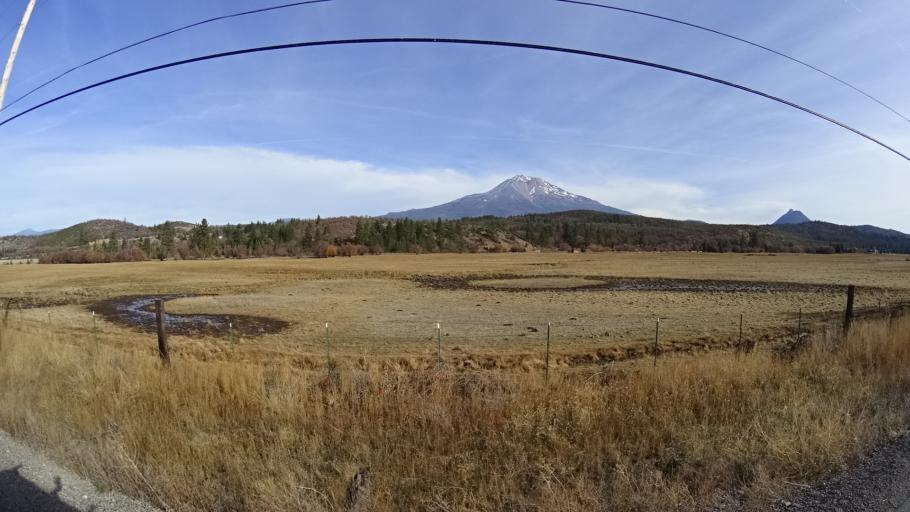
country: US
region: California
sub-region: Siskiyou County
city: Weed
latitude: 41.4275
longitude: -122.4372
